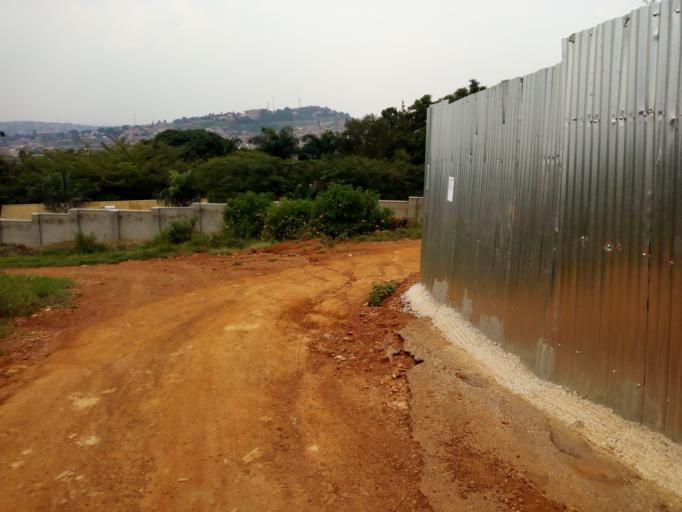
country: UG
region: Central Region
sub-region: Wakiso District
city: Kireka
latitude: 0.3283
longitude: 32.6328
